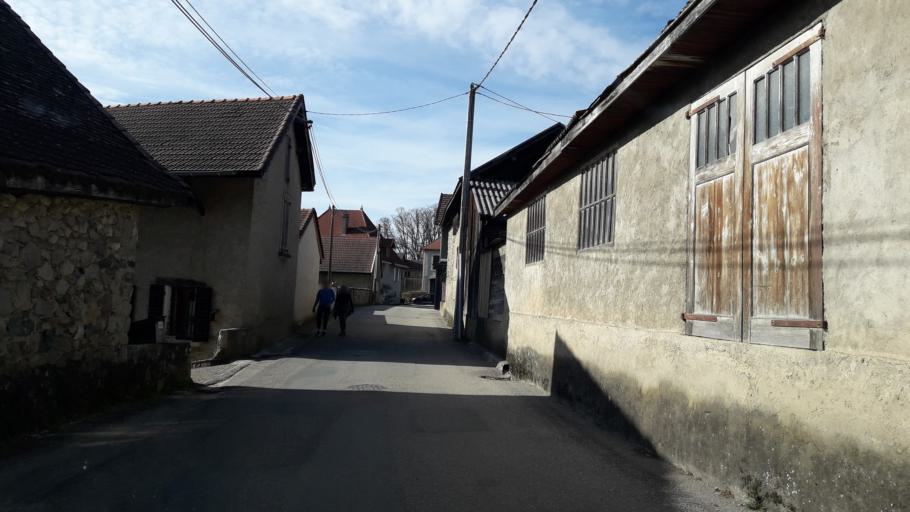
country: FR
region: Rhone-Alpes
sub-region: Departement de l'Isere
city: Herbeys
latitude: 45.1383
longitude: 5.7941
